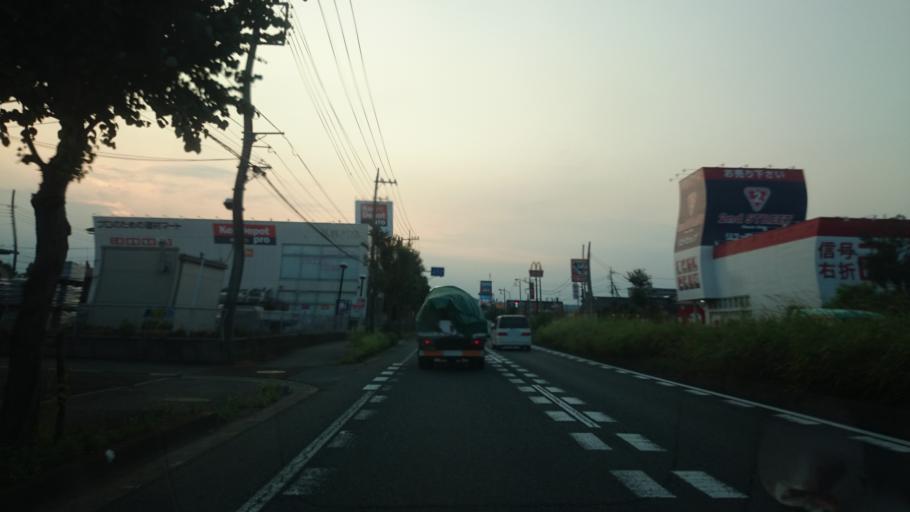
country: JP
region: Saitama
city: Hasuda
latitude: 35.9535
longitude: 139.6642
